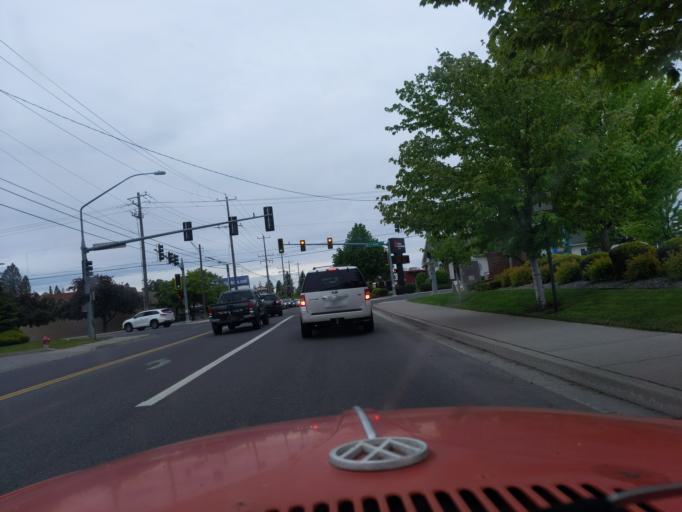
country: US
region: Washington
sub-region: Spokane County
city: Spokane
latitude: 47.6018
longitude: -117.3685
